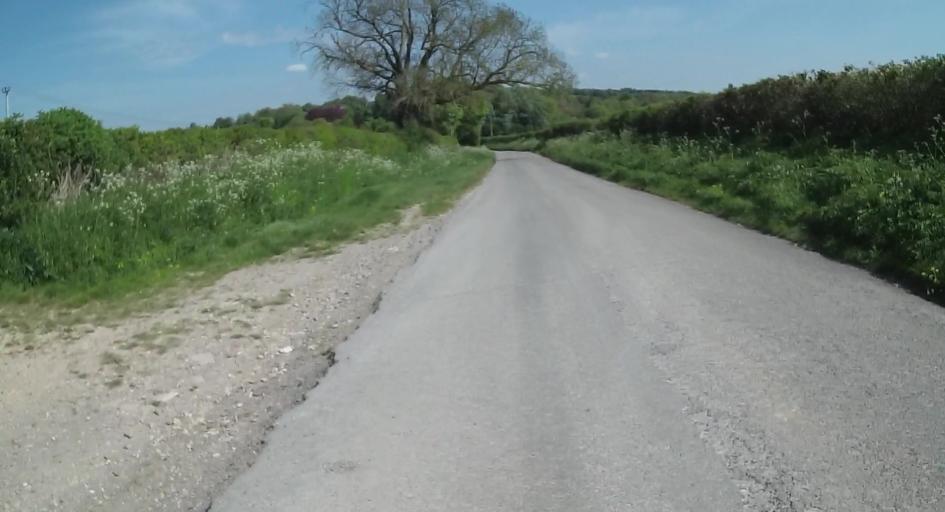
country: GB
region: England
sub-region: Hampshire
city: Andover
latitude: 51.1689
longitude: -1.3865
